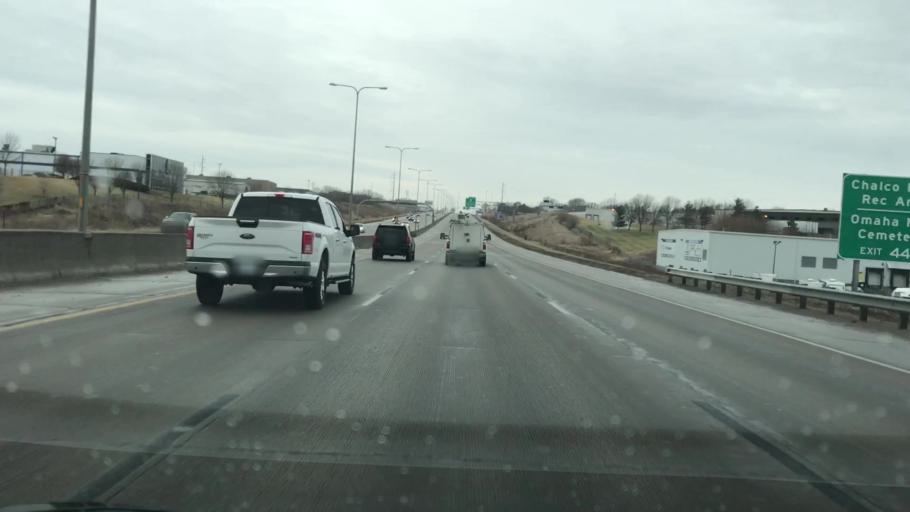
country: US
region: Nebraska
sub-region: Sarpy County
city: Chalco
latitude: 41.1749
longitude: -96.1219
